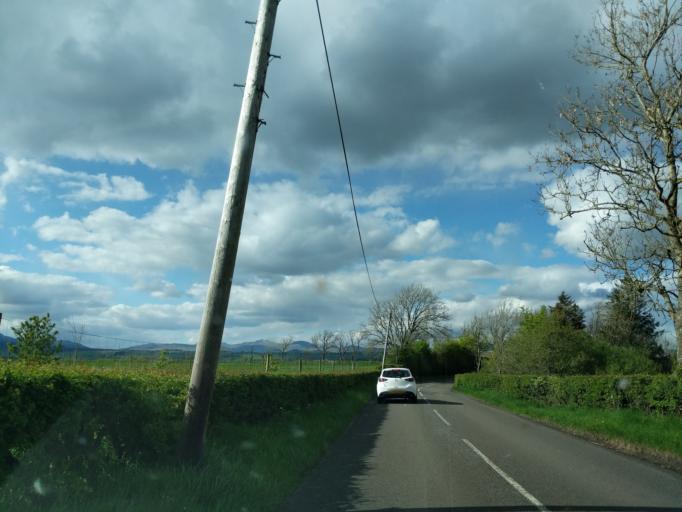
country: GB
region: Scotland
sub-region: Stirling
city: Doune
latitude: 56.1437
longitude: -4.1472
